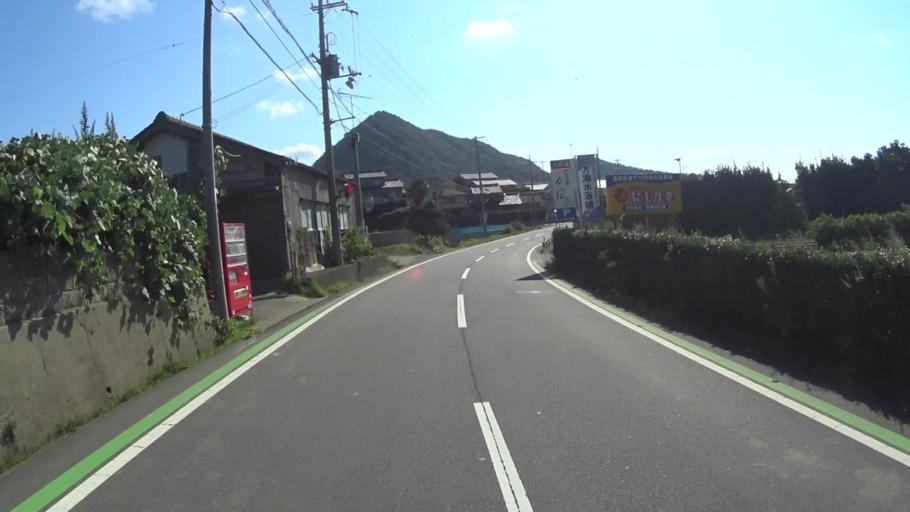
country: JP
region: Kyoto
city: Miyazu
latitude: 35.7220
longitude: 135.0835
